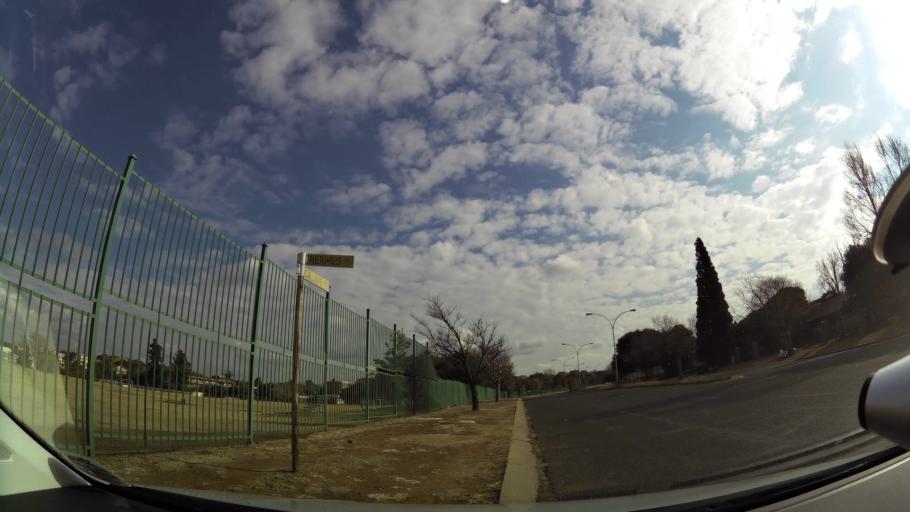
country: ZA
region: Orange Free State
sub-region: Mangaung Metropolitan Municipality
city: Bloemfontein
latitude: -29.0749
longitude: 26.2342
